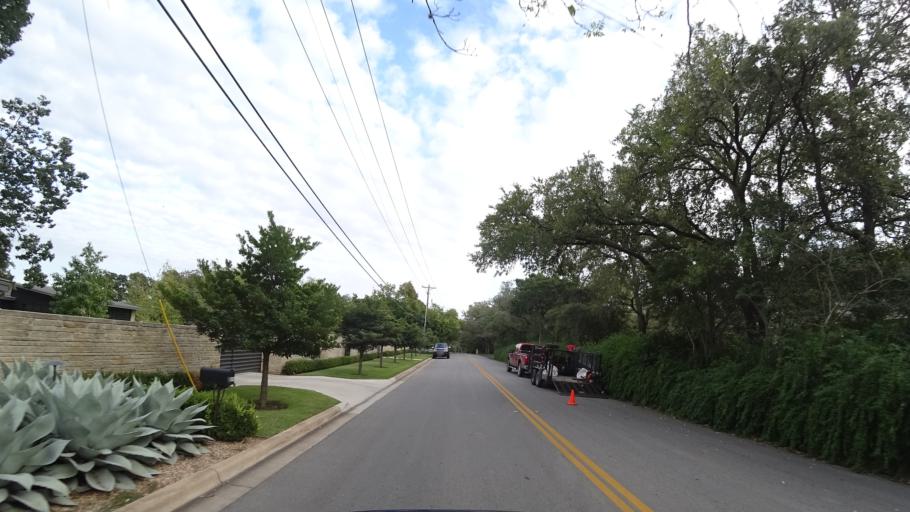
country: US
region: Texas
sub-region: Travis County
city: Rollingwood
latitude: 30.2814
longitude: -97.7837
